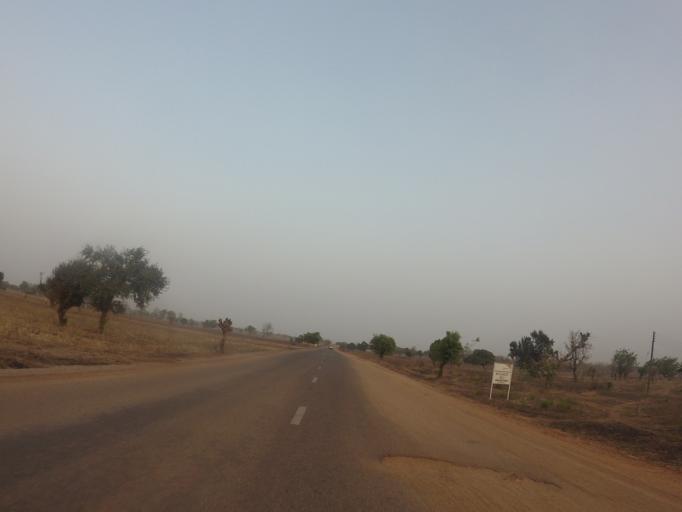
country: GH
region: Northern
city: Tamale
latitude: 9.4421
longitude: -1.1063
